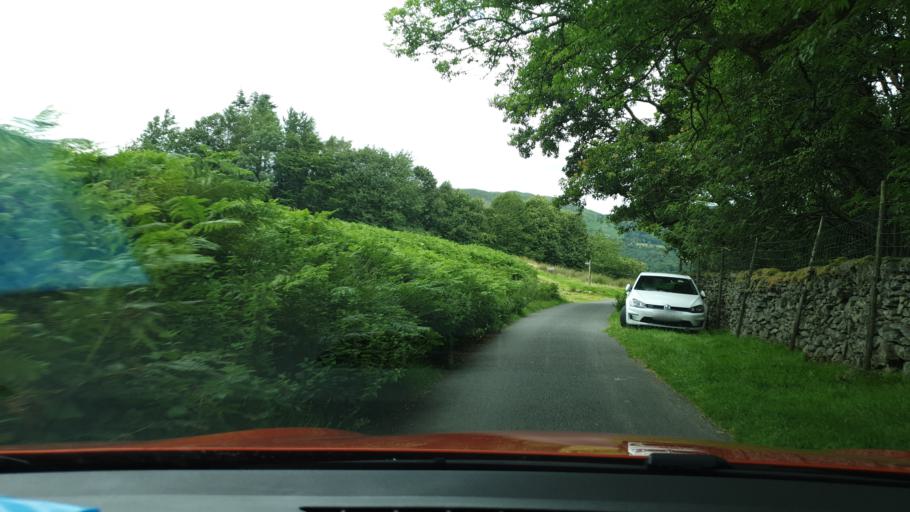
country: GB
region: England
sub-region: Cumbria
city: Ambleside
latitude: 54.5674
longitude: -2.8925
